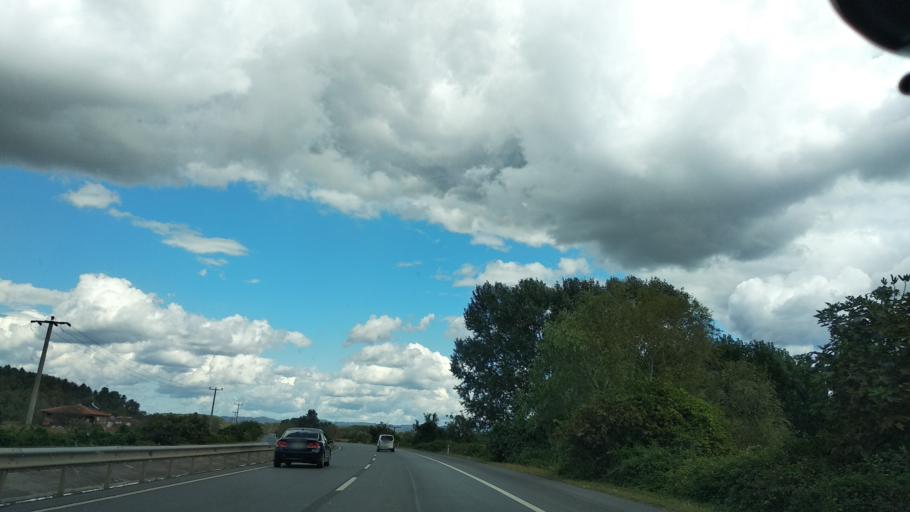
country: TR
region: Sakarya
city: Sogutlu
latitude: 40.8330
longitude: 30.4780
